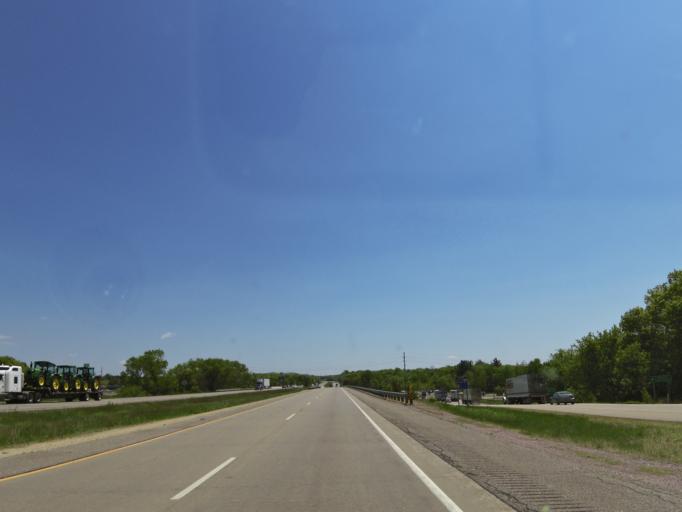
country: US
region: Wisconsin
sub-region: Juneau County
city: Mauston
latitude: 43.7986
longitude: -90.0587
